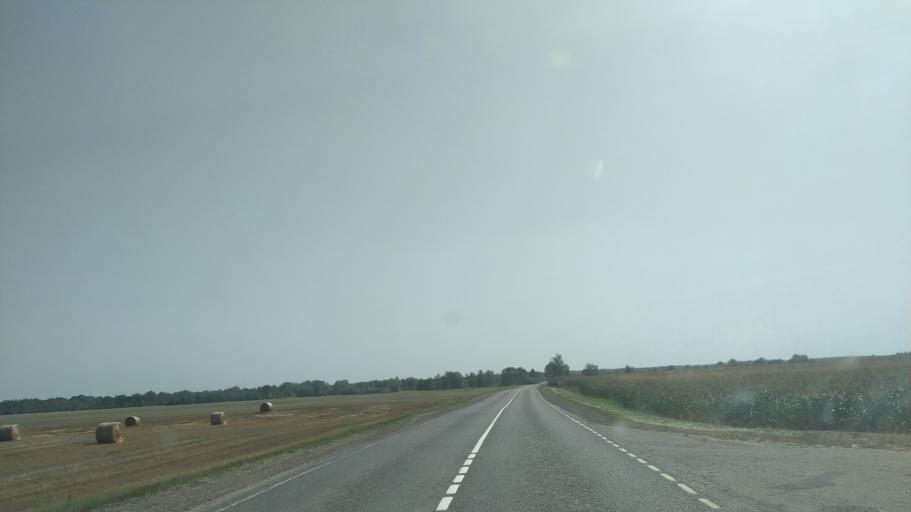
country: BY
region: Brest
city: Byaroza
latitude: 52.4328
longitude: 24.9805
